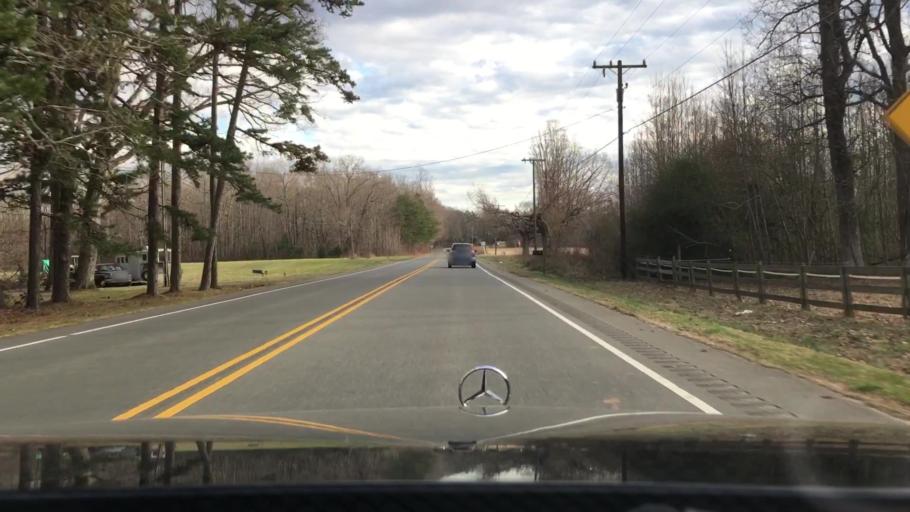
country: US
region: North Carolina
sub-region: Orange County
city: Hillsborough
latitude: 36.1529
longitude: -79.1257
